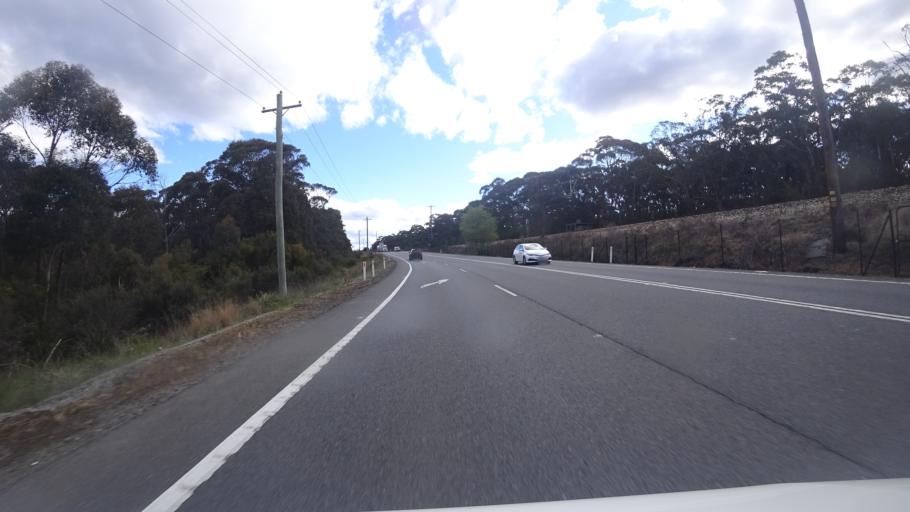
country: AU
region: New South Wales
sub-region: Blue Mountains Municipality
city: Blackheath
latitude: -33.6537
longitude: 150.2824
